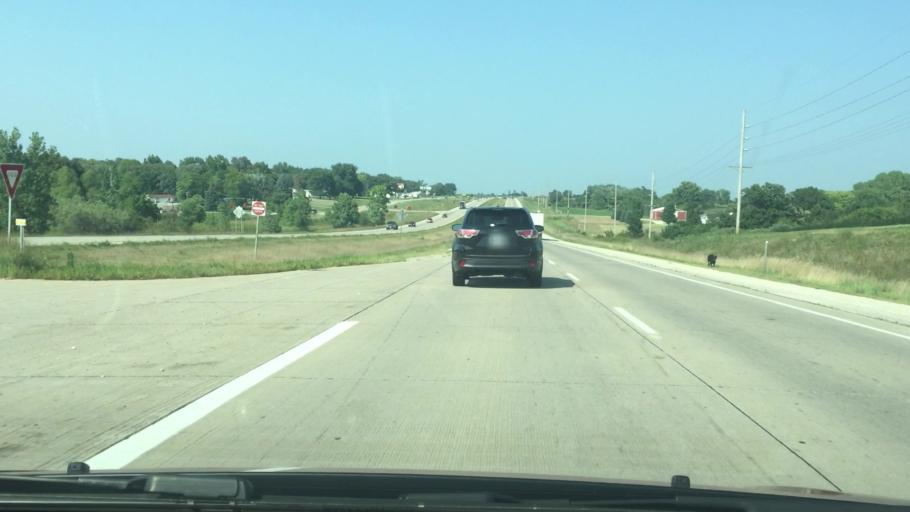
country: US
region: Iowa
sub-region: Muscatine County
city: Muscatine
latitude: 41.4673
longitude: -91.0044
